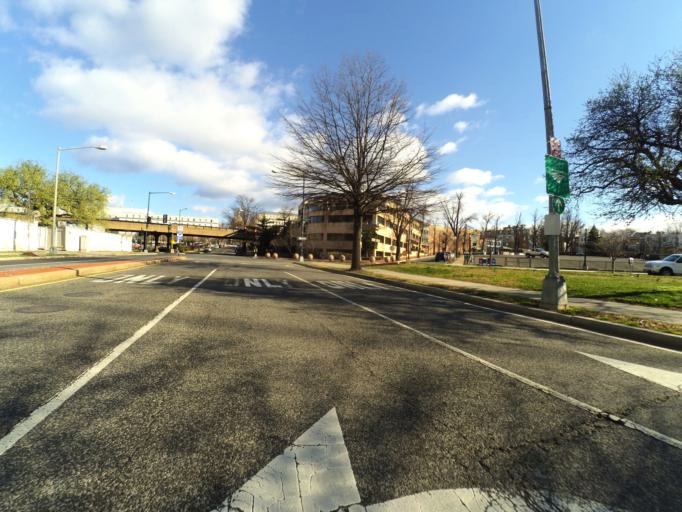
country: US
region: Washington, D.C.
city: Washington, D.C.
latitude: 38.8833
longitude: -77.0090
